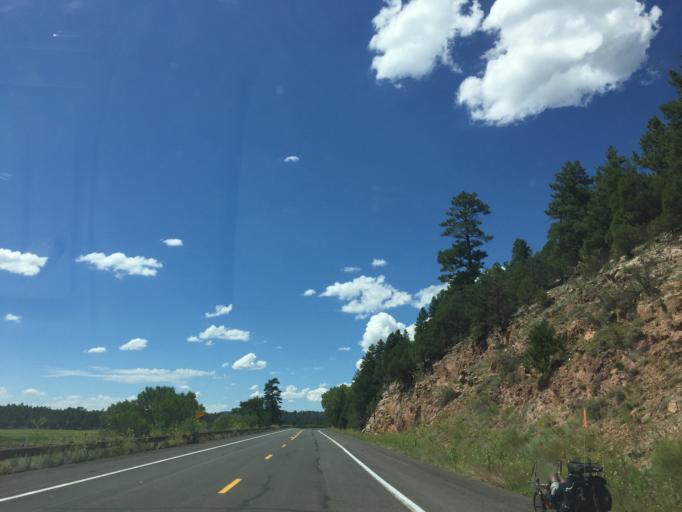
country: US
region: Arizona
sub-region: Coconino County
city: Mountainaire
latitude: 35.1084
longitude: -111.5732
